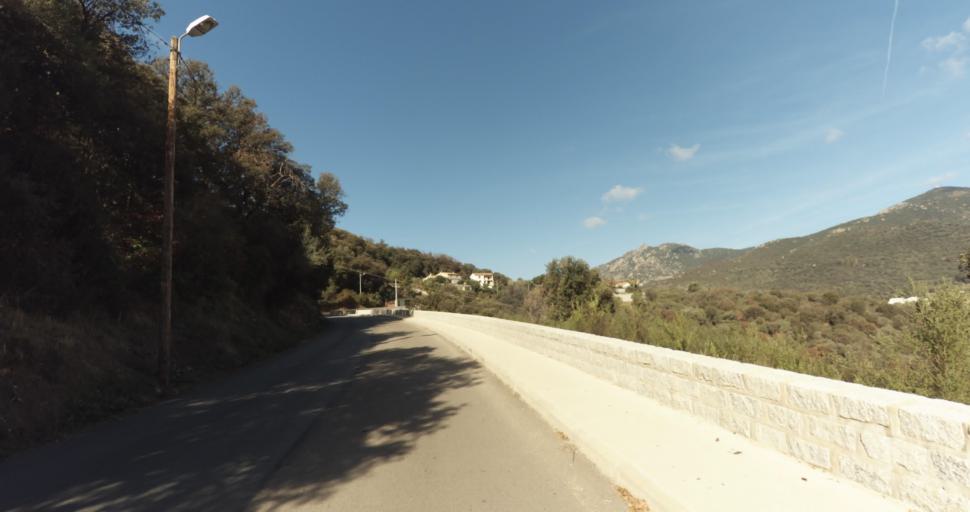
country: FR
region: Corsica
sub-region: Departement de la Corse-du-Sud
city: Ajaccio
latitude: 41.9244
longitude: 8.7213
